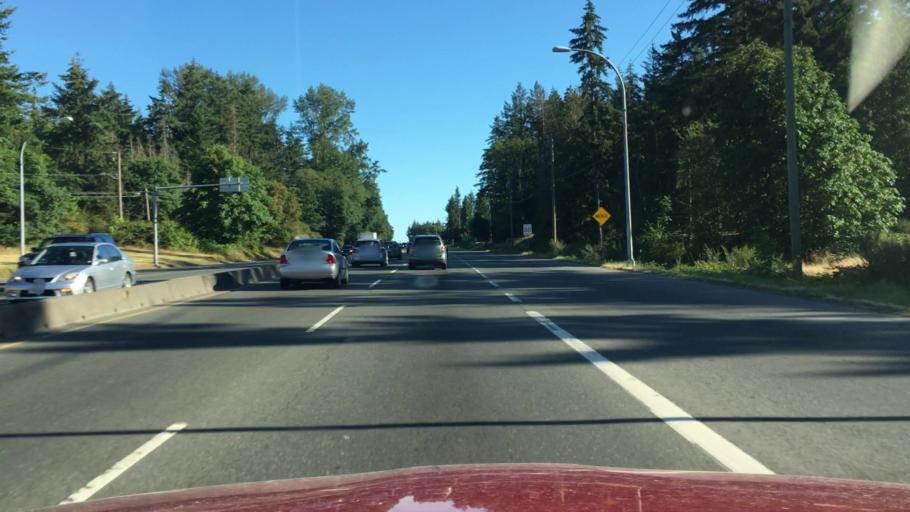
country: CA
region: British Columbia
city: Victoria
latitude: 48.5381
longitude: -123.3893
